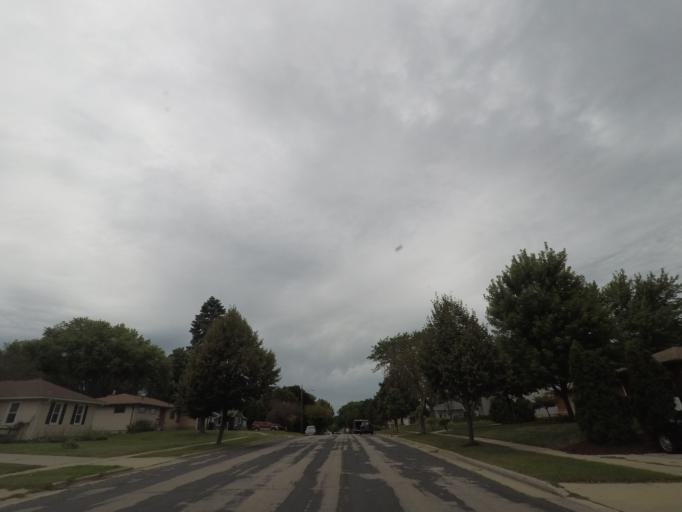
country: US
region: Wisconsin
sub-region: Dane County
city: Middleton
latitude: 43.0947
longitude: -89.4956
